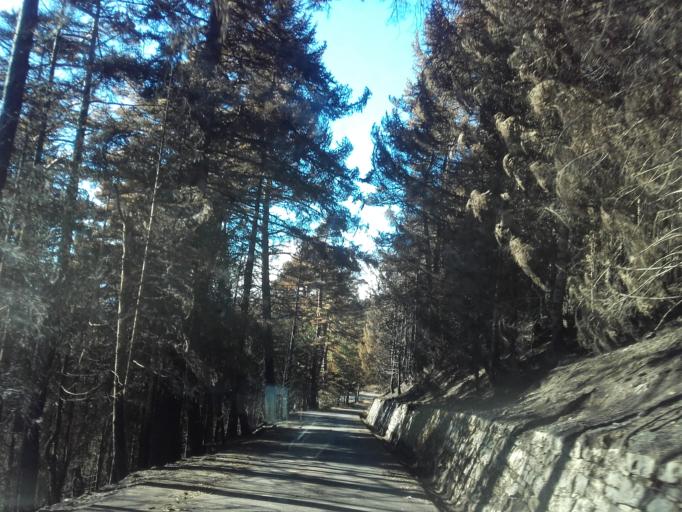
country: IT
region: Piedmont
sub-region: Provincia di Torino
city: Mompantero
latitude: 45.1669
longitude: 7.0430
